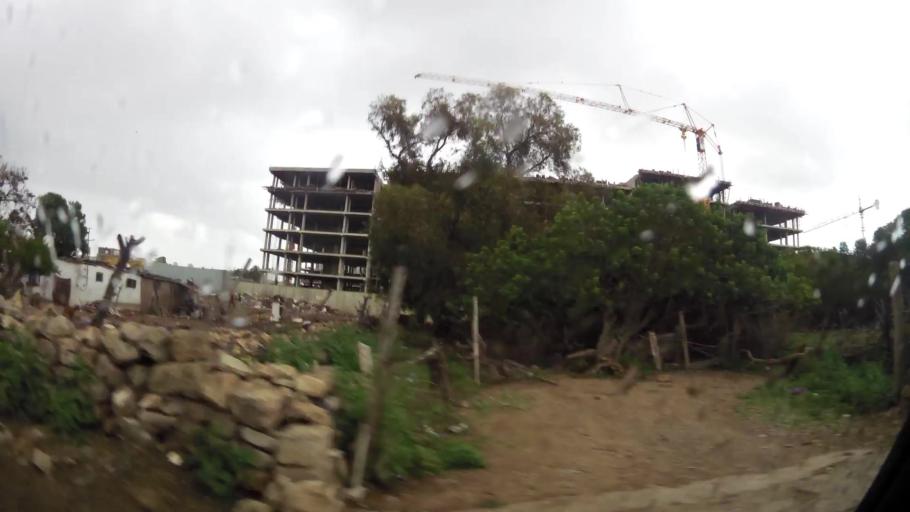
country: MA
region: Grand Casablanca
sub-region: Casablanca
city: Casablanca
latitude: 33.5790
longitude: -7.6838
